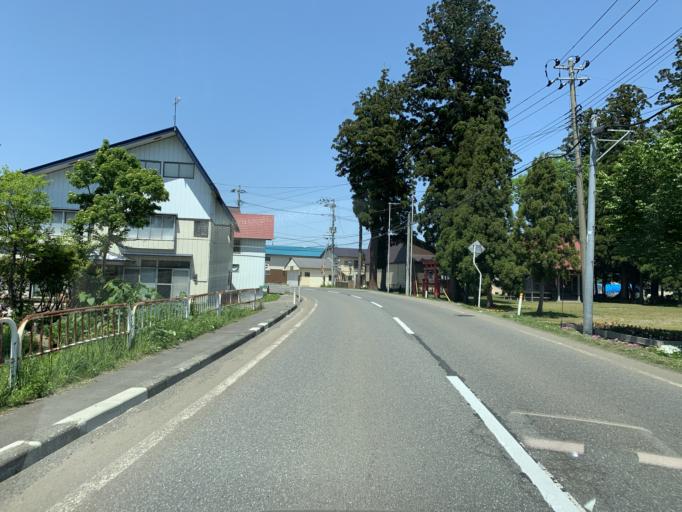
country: JP
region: Akita
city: Yokotemachi
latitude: 39.3910
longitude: 140.7586
